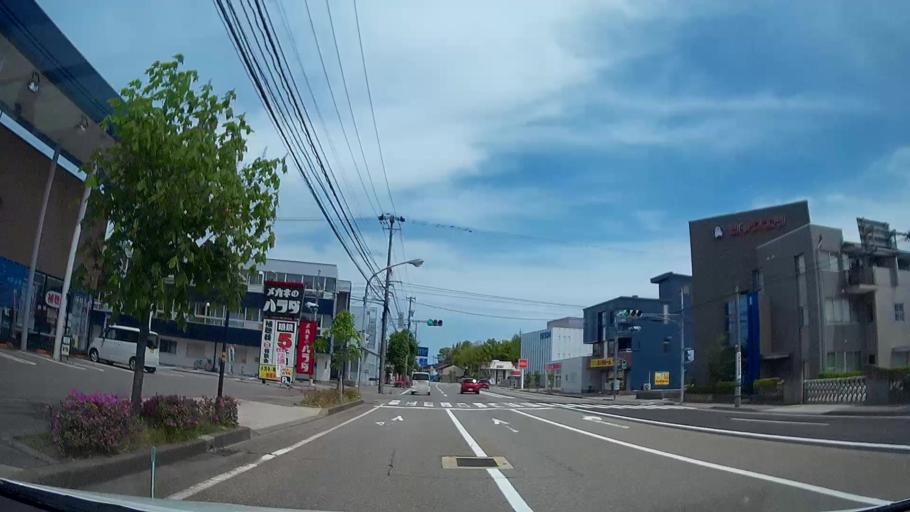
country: JP
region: Ishikawa
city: Kanazawa-shi
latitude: 36.5844
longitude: 136.6482
